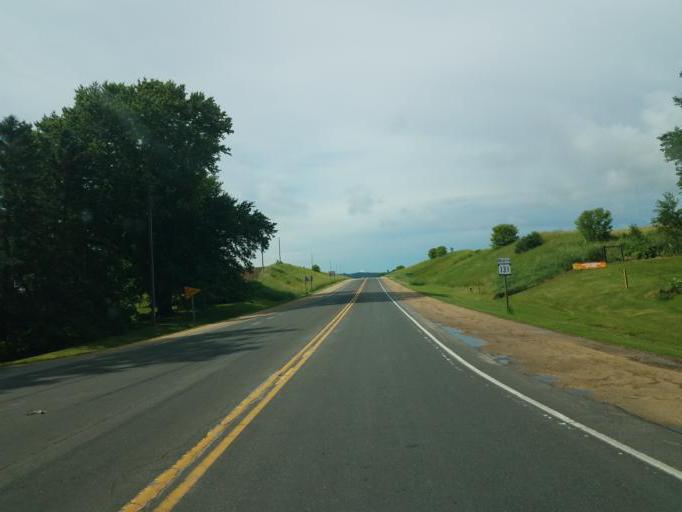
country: US
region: Wisconsin
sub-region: Monroe County
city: Tomah
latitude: 43.8332
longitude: -90.4739
